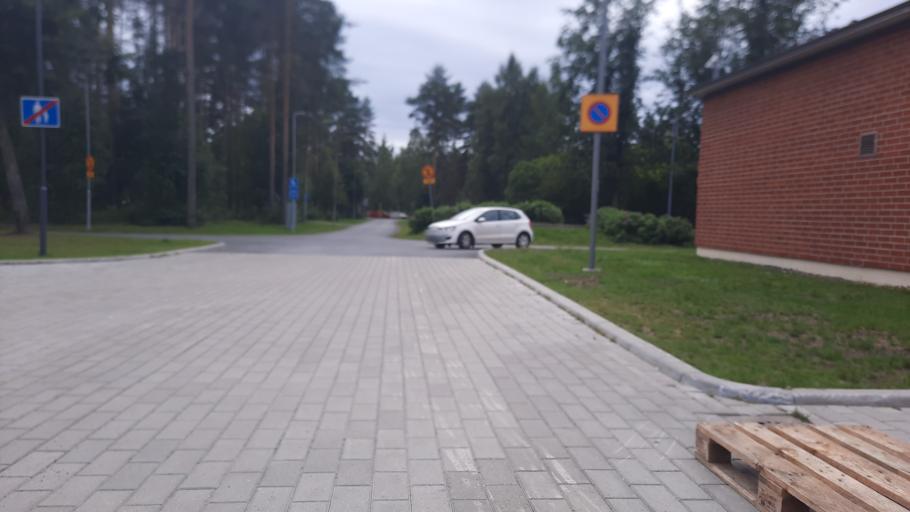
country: FI
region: North Karelia
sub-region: Joensuu
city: Joensuu
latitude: 62.6138
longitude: 29.8186
